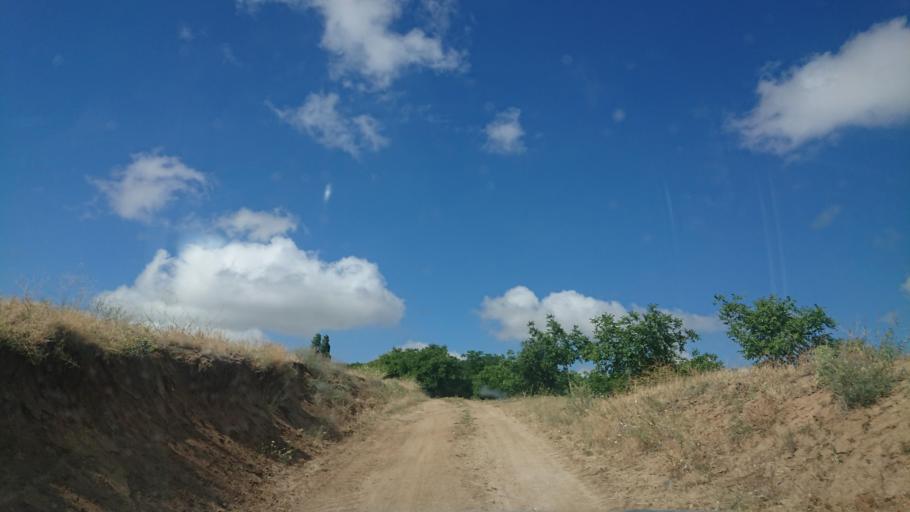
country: TR
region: Aksaray
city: Agacoren
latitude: 38.8474
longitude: 33.9375
